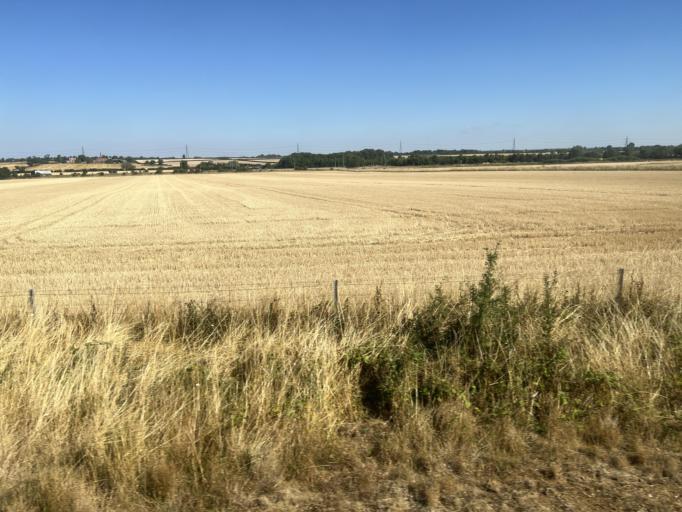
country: GB
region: England
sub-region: Lincolnshire
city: Heckington
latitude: 52.9832
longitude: -0.3245
